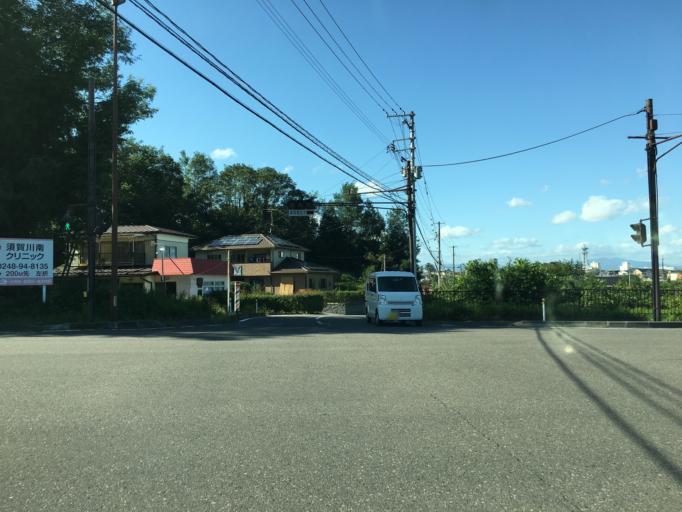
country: JP
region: Fukushima
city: Sukagawa
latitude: 37.2775
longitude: 140.3772
